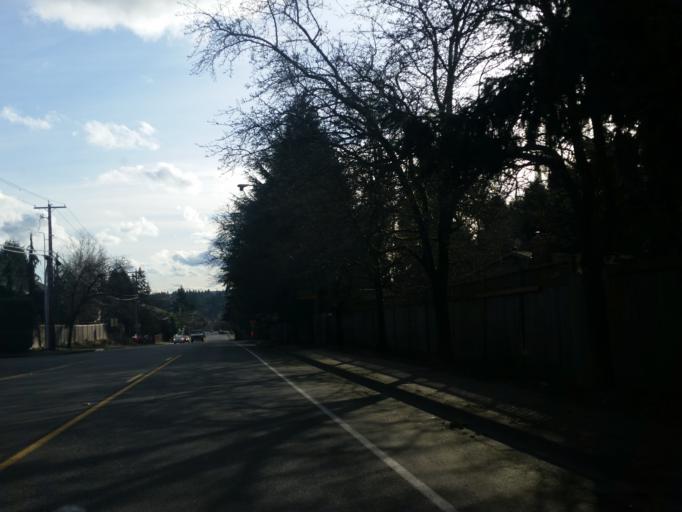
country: US
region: Washington
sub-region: King County
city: Kingsgate
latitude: 47.7220
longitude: -122.1642
